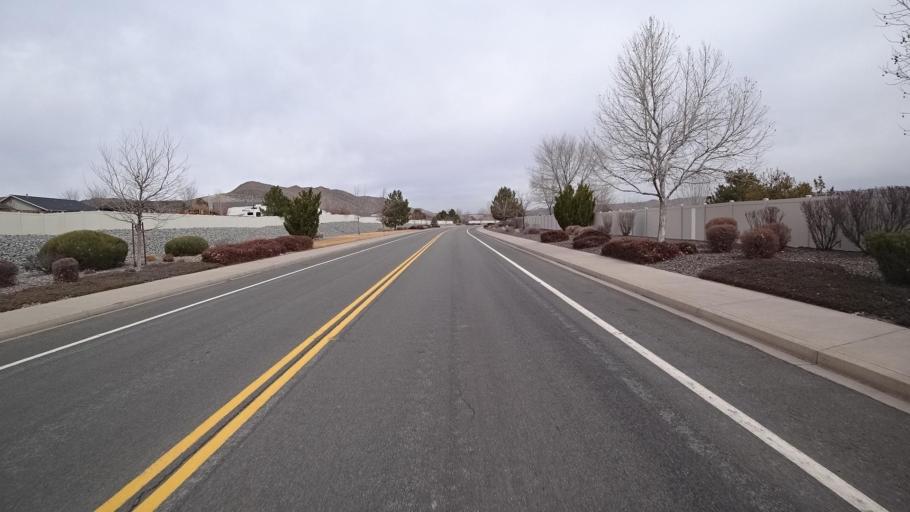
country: US
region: Nevada
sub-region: Washoe County
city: Spanish Springs
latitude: 39.6687
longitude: -119.7214
